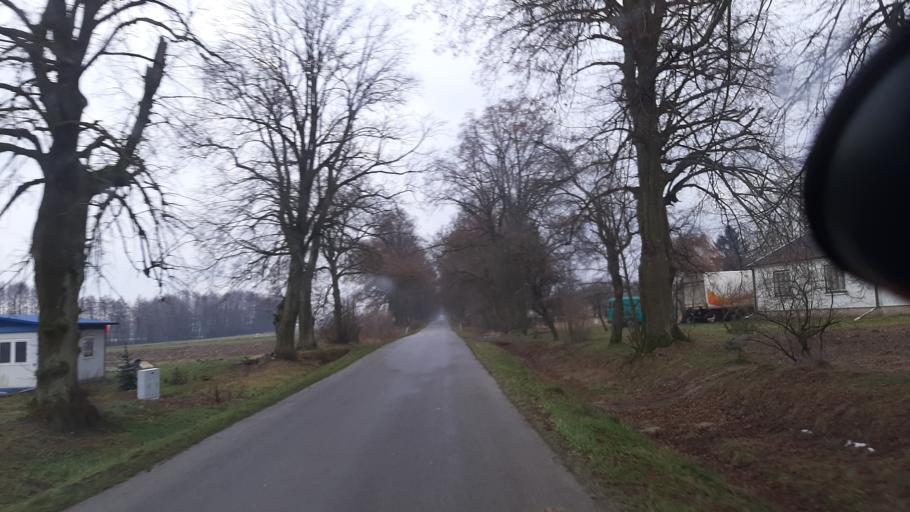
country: PL
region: Lublin Voivodeship
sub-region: Powiat lubelski
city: Jastkow
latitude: 51.3463
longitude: 22.5223
